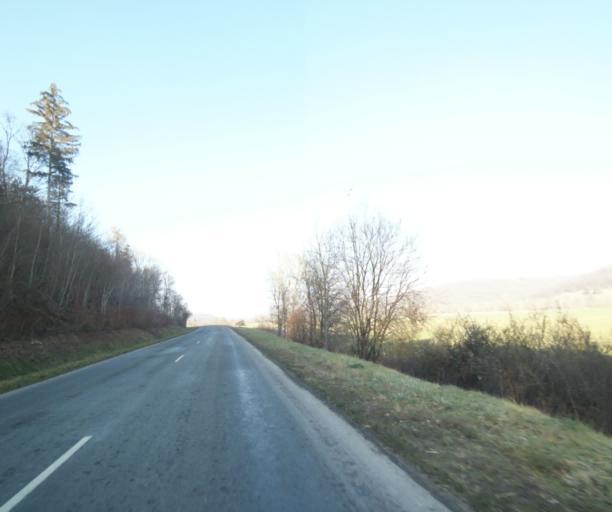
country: FR
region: Champagne-Ardenne
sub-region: Departement de la Haute-Marne
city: Chevillon
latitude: 48.4993
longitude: 5.1192
